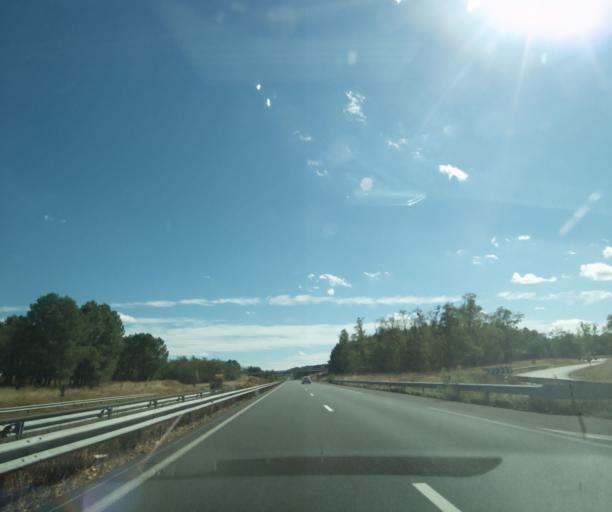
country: FR
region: Aquitaine
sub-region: Departement du Lot-et-Garonne
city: Damazan
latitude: 44.2837
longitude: 0.2673
